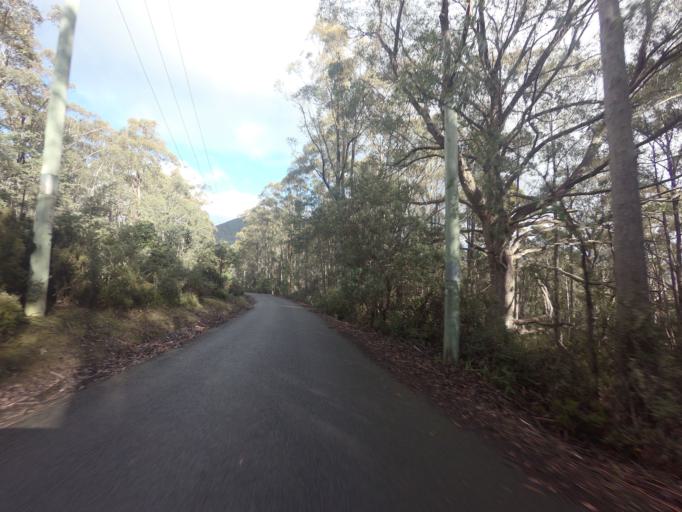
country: AU
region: Tasmania
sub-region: Glenorchy
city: Berriedale
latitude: -42.8430
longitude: 147.1480
